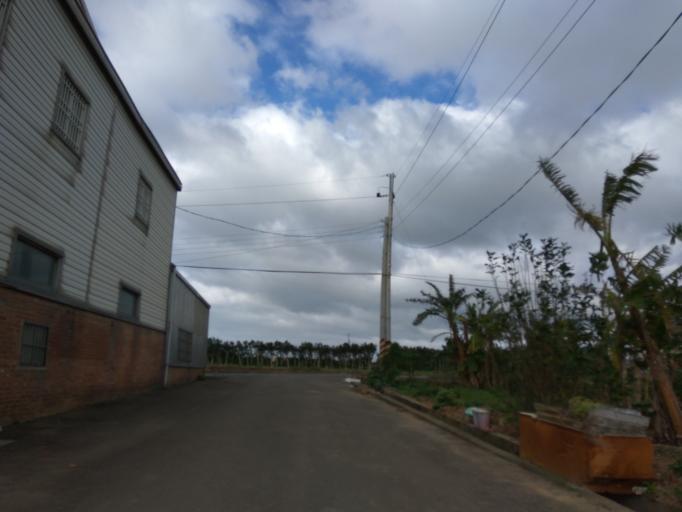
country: TW
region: Taiwan
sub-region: Hsinchu
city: Zhubei
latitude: 24.9711
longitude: 121.0890
